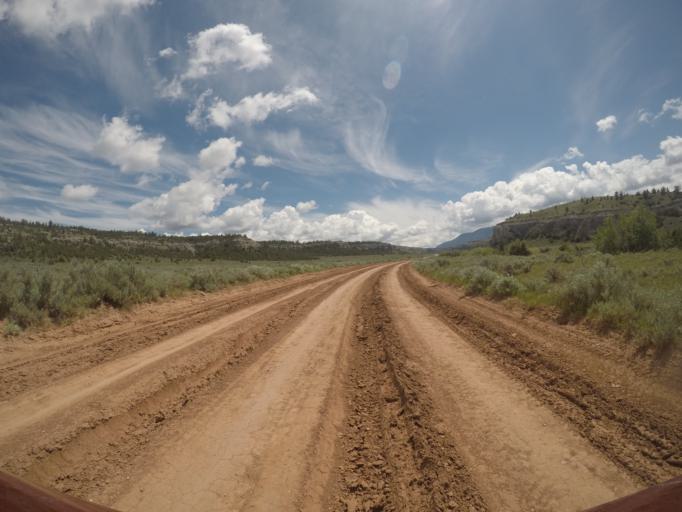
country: US
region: Montana
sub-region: Yellowstone County
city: Laurel
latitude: 45.2436
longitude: -108.6449
